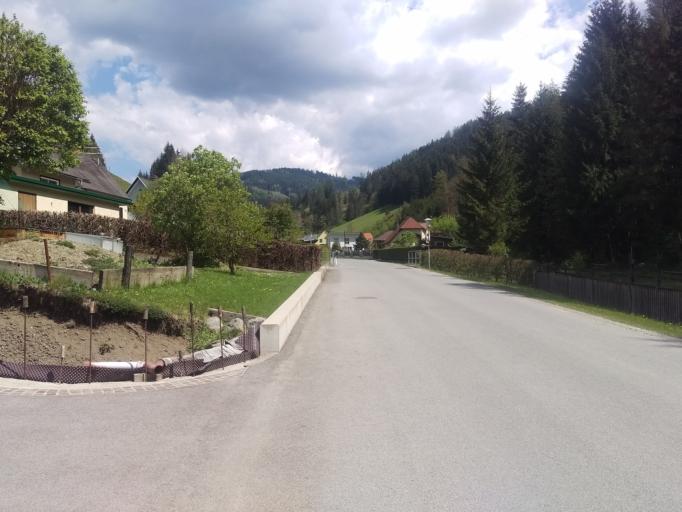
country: AT
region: Styria
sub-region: Politischer Bezirk Bruck-Muerzzuschlag
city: Allerheiligen im Muerztal
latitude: 47.3954
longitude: 15.4327
